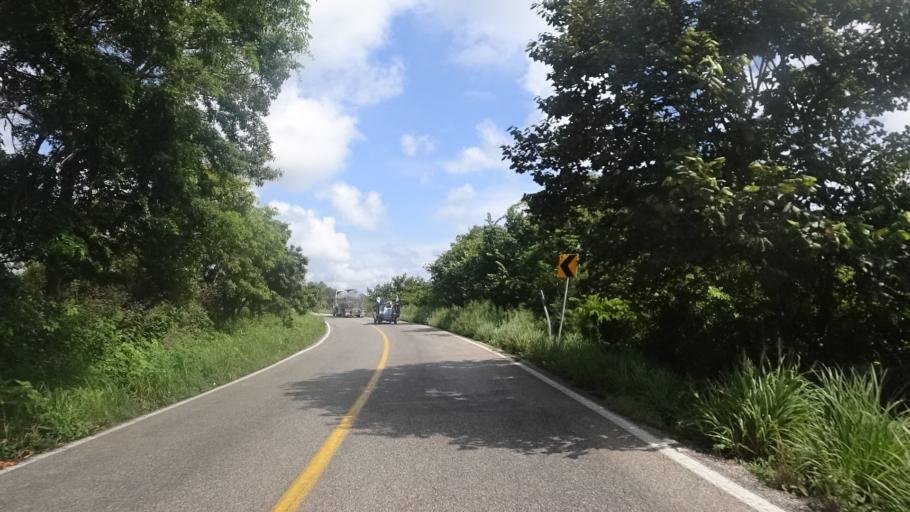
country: MX
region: Chiapas
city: Palenque
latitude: 17.6079
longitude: -92.0238
